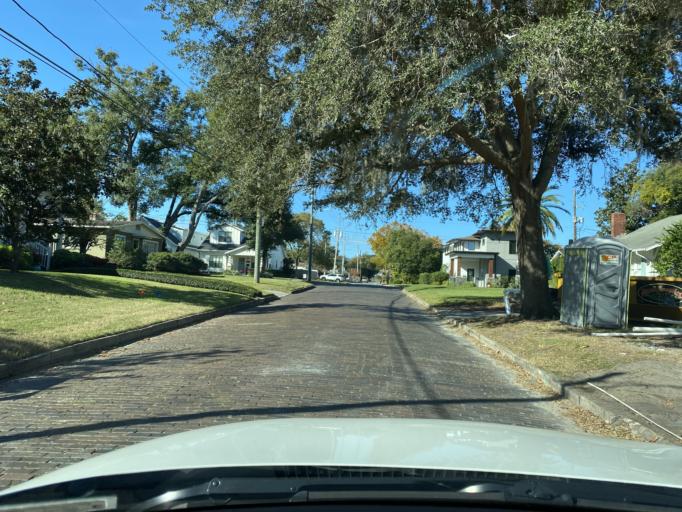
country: US
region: Florida
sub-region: Orange County
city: Orlando
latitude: 28.5626
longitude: -81.3877
